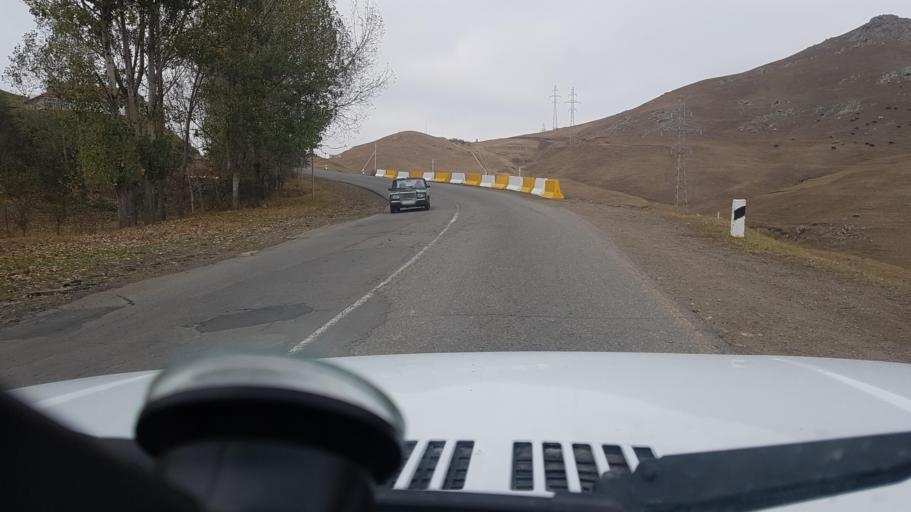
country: AZ
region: Gadabay Rayon
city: Ariqdam
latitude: 40.6119
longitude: 45.8129
